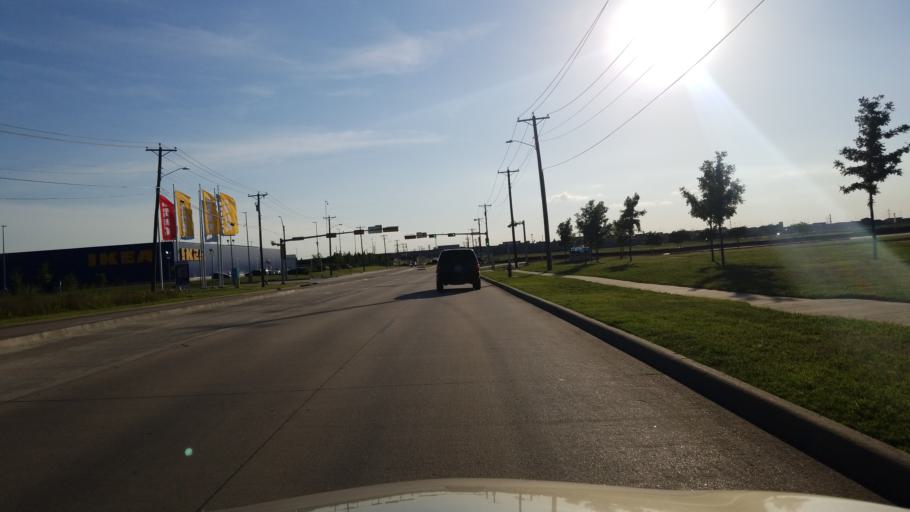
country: US
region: Texas
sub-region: Dallas County
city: Grand Prairie
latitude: 32.6918
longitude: -97.0196
